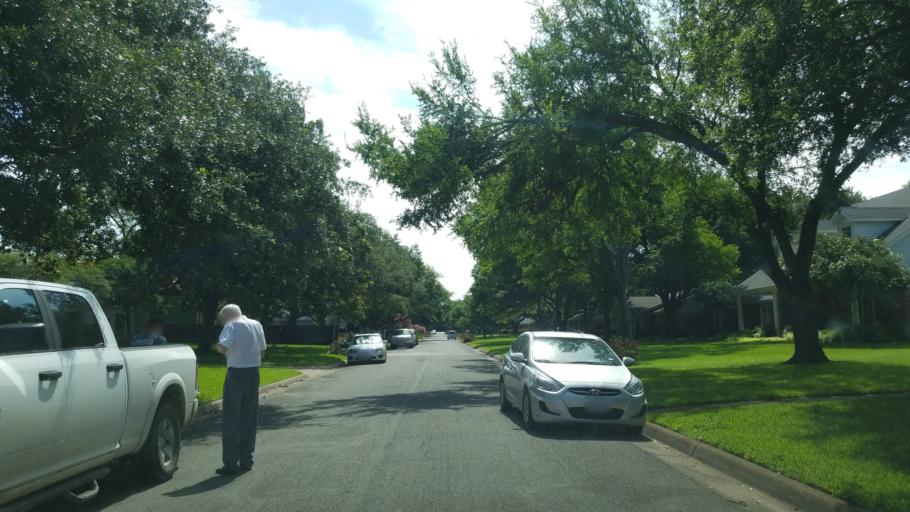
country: US
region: Texas
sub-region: Dallas County
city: Addison
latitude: 32.9069
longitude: -96.8422
